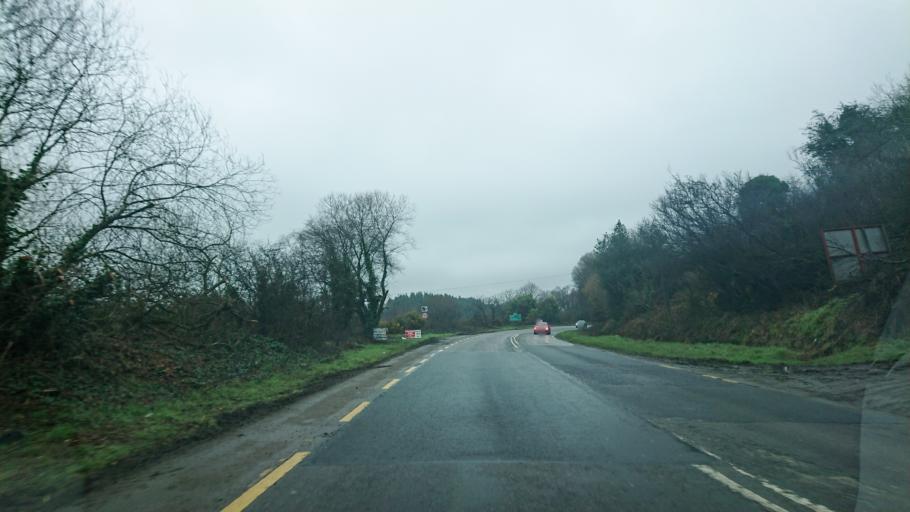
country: IE
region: Munster
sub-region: County Cork
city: Bandon
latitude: 51.7545
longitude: -8.7153
